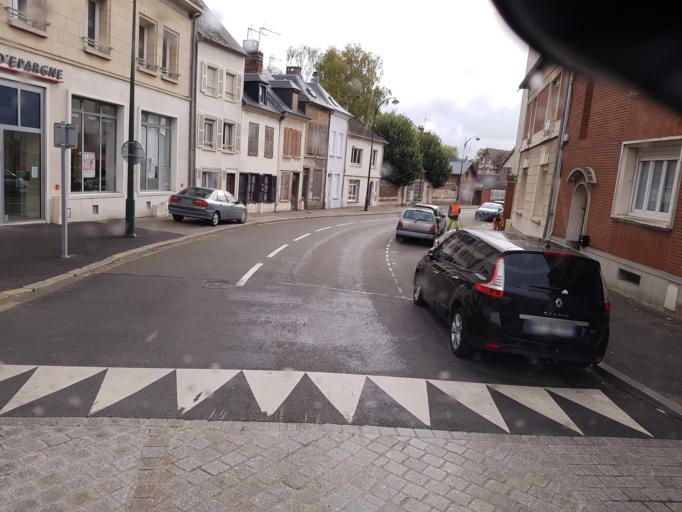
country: FR
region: Picardie
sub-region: Departement de l'Oise
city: Breteuil
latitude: 49.6336
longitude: 2.2960
